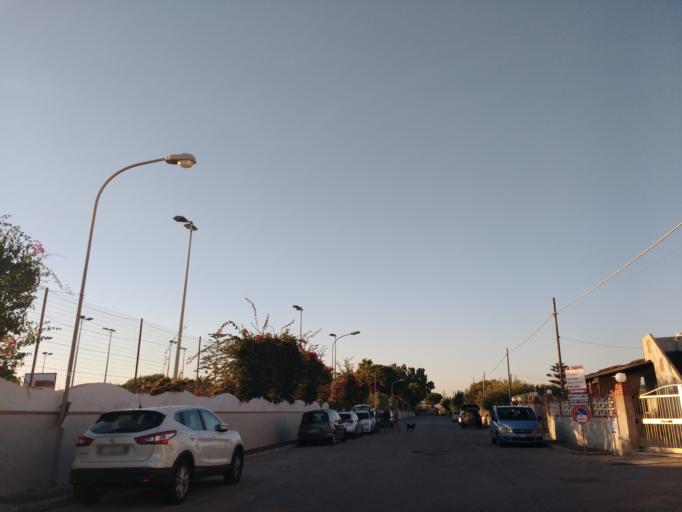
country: IT
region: Sicily
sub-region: Ragusa
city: Ispica
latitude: 36.7231
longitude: 14.9158
